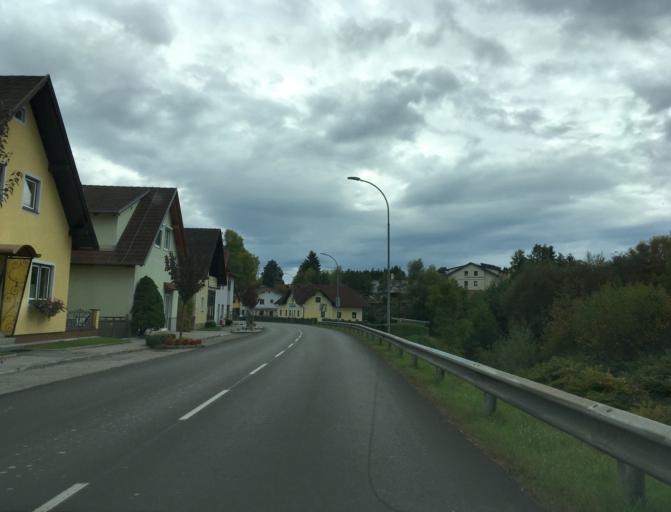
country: AT
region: Lower Austria
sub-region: Politischer Bezirk Wiener Neustadt
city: Bad Schonau
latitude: 47.5185
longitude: 16.1933
